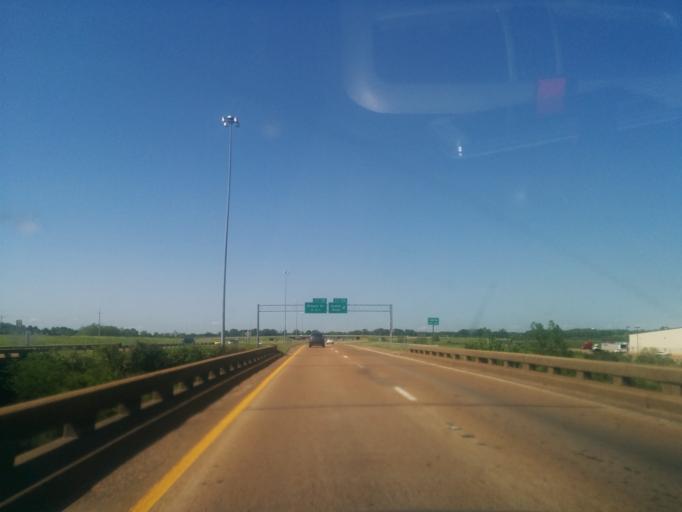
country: US
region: Mississippi
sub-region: Madison County
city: Madison
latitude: 32.5313
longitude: -90.0952
